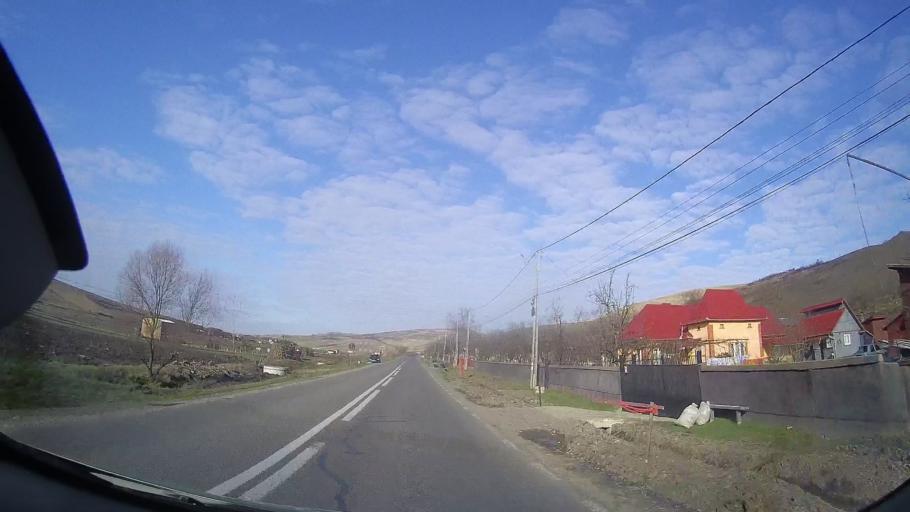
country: RO
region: Cluj
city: Caianu Mic
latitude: 46.8013
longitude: 23.8741
